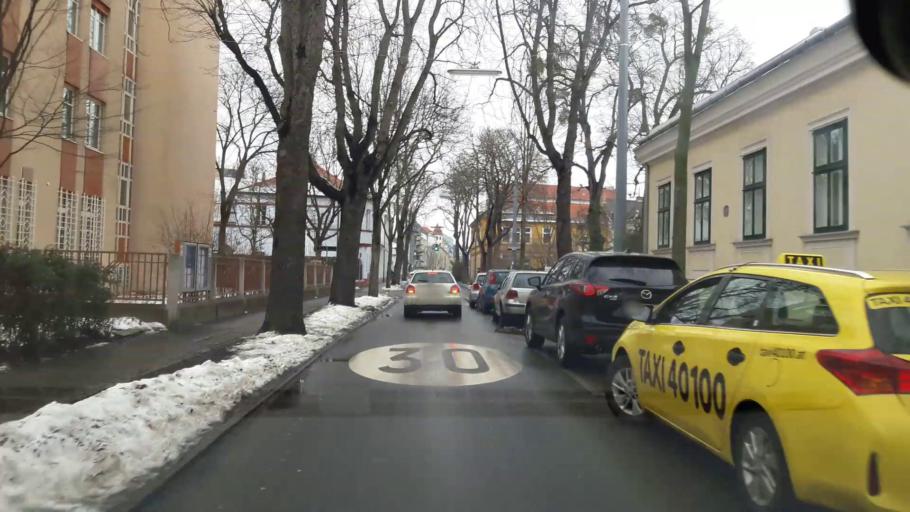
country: AT
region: Lower Austria
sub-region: Politischer Bezirk Modling
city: Perchtoldsdorf
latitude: 48.1862
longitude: 16.2843
